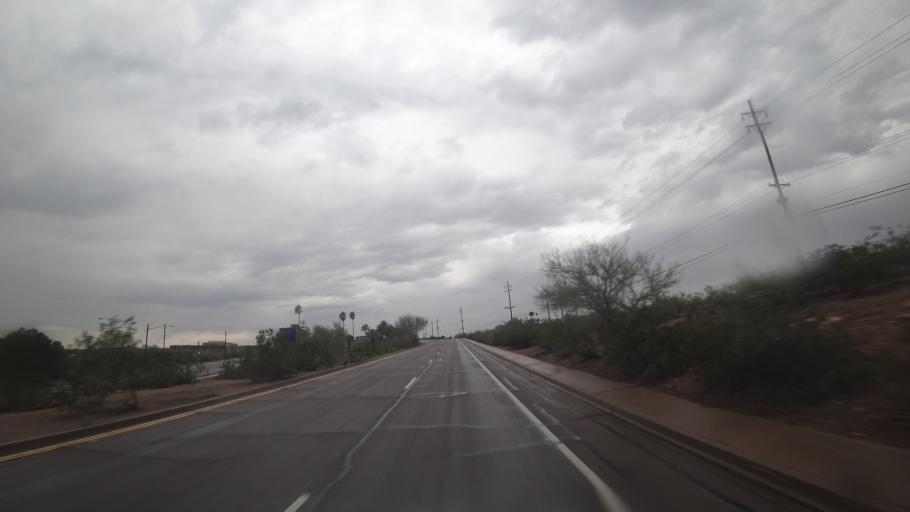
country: US
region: Arizona
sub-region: Maricopa County
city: Tempe Junction
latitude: 33.4412
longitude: -111.9456
